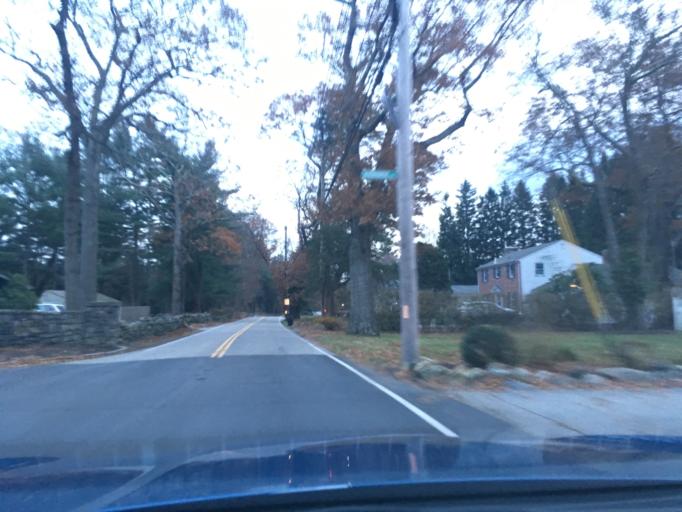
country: US
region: Rhode Island
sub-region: Kent County
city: East Greenwich
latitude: 41.6800
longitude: -71.4602
